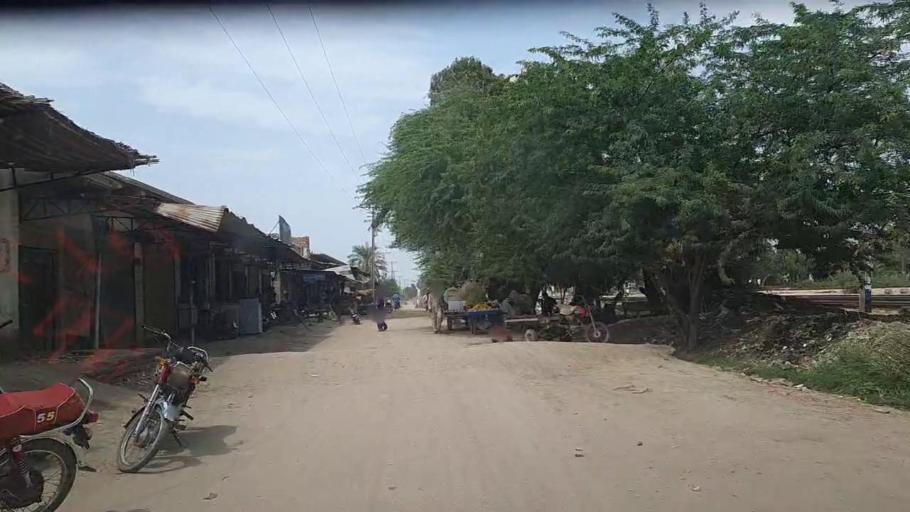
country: PK
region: Sindh
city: Bhiria
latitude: 26.8922
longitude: 68.2850
